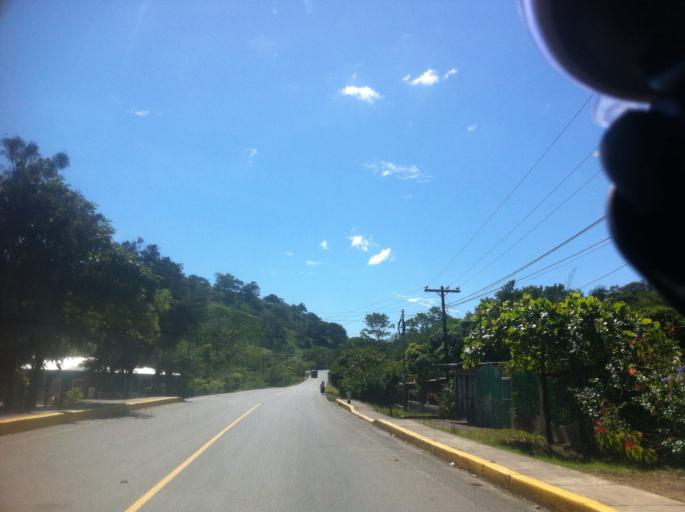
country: NI
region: Matagalpa
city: San Ramon
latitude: 12.9232
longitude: -85.8406
